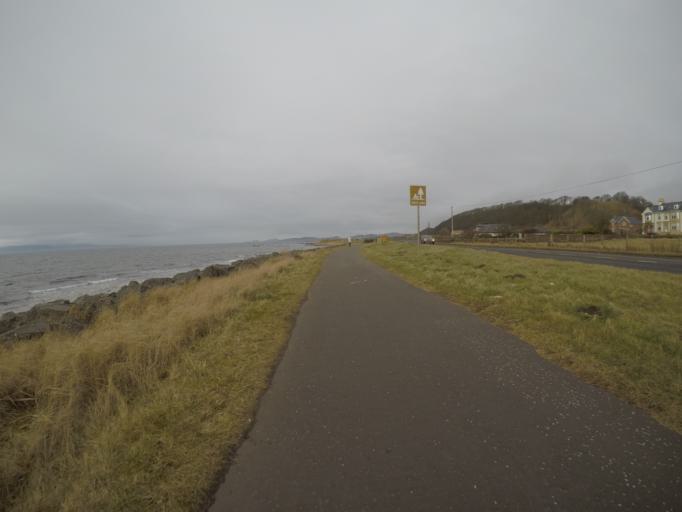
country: GB
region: Scotland
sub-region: North Ayrshire
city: West Kilbride
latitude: 55.6665
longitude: -4.8402
